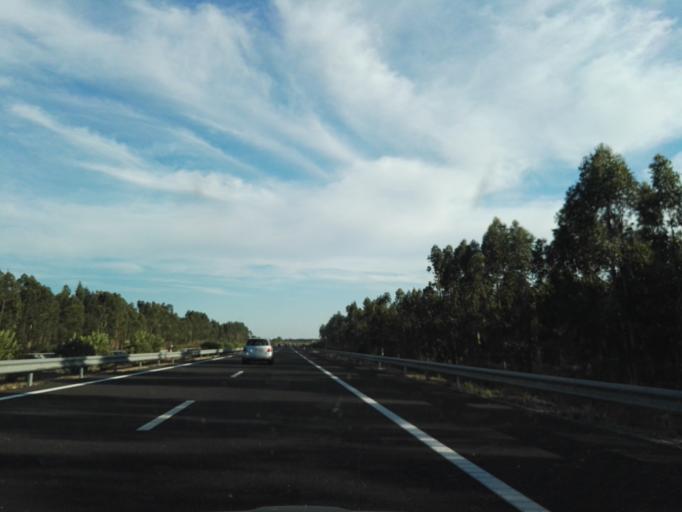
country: PT
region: Santarem
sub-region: Benavente
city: Poceirao
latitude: 38.7951
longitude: -8.6933
